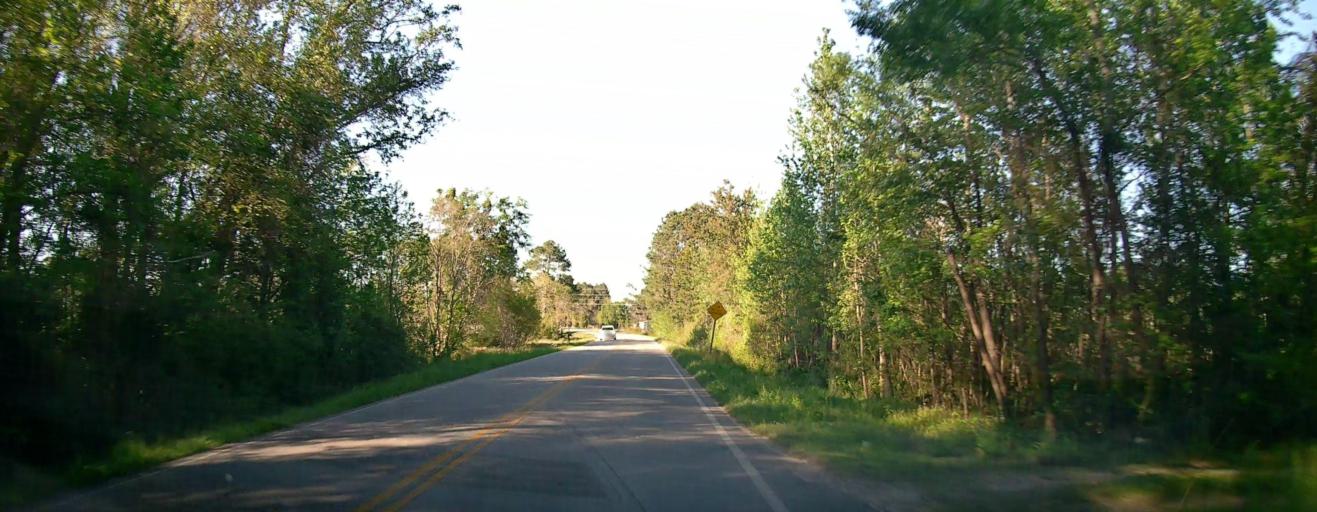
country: US
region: Georgia
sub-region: Ben Hill County
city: Fitzgerald
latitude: 31.7378
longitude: -83.2350
